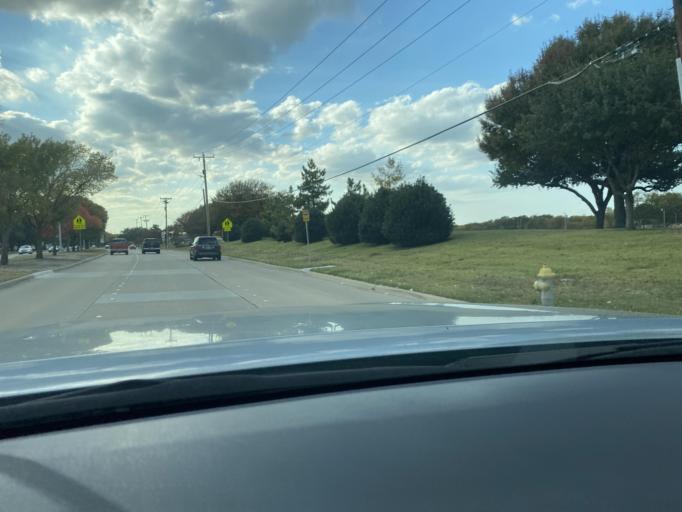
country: US
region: Texas
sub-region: Dallas County
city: Addison
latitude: 33.0167
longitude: -96.8069
